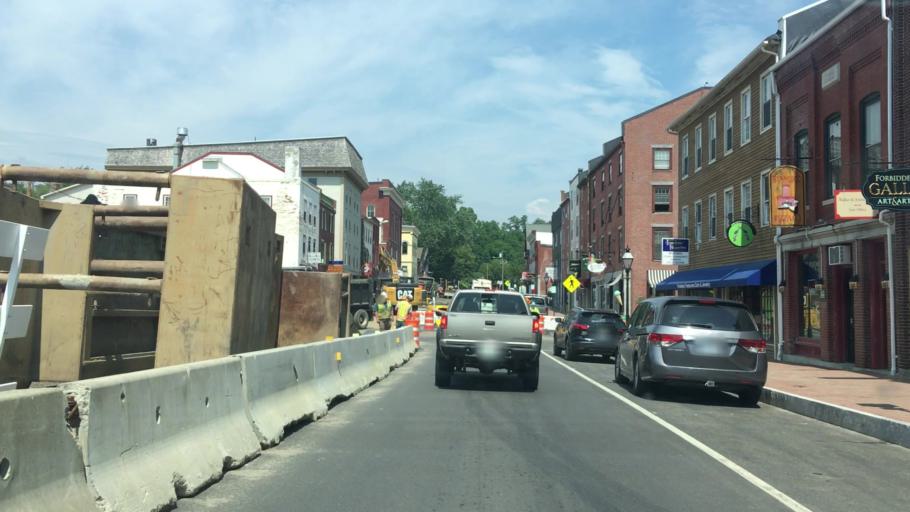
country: US
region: Maine
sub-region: Kennebec County
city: Hallowell
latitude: 44.2855
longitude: -69.7902
